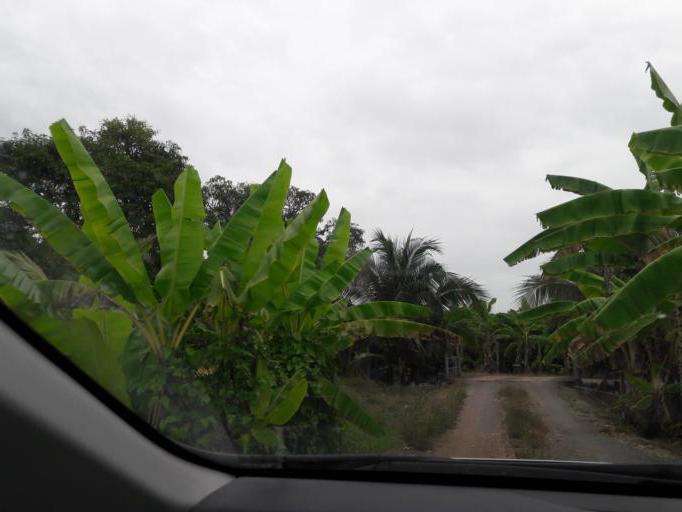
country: TH
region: Samut Sakhon
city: Ban Phaeo
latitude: 13.5927
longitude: 100.0370
